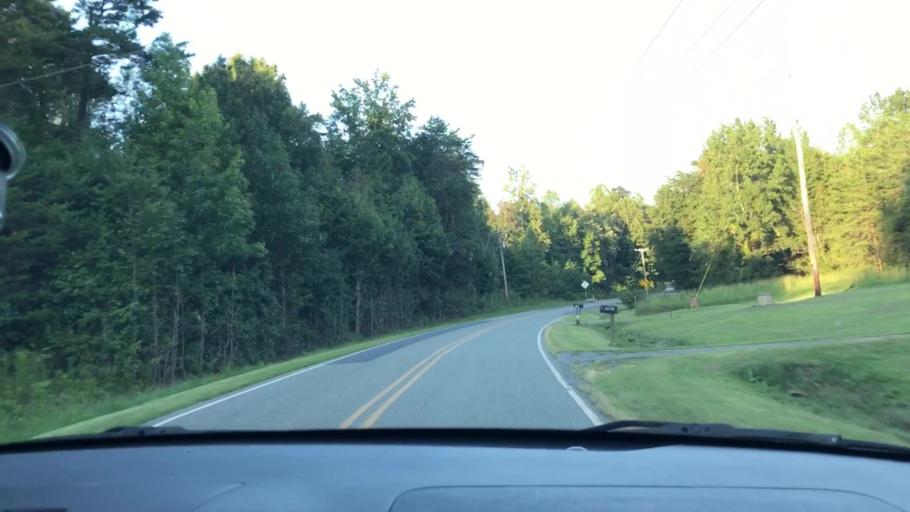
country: US
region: North Carolina
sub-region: Randolph County
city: Franklinville
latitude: 35.7994
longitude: -79.6645
